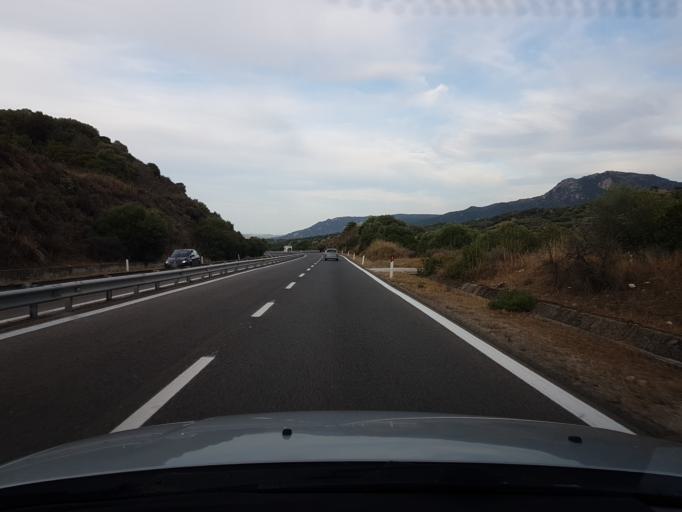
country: IT
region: Sardinia
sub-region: Provincia di Nuoro
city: Orune
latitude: 40.3619
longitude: 9.3581
